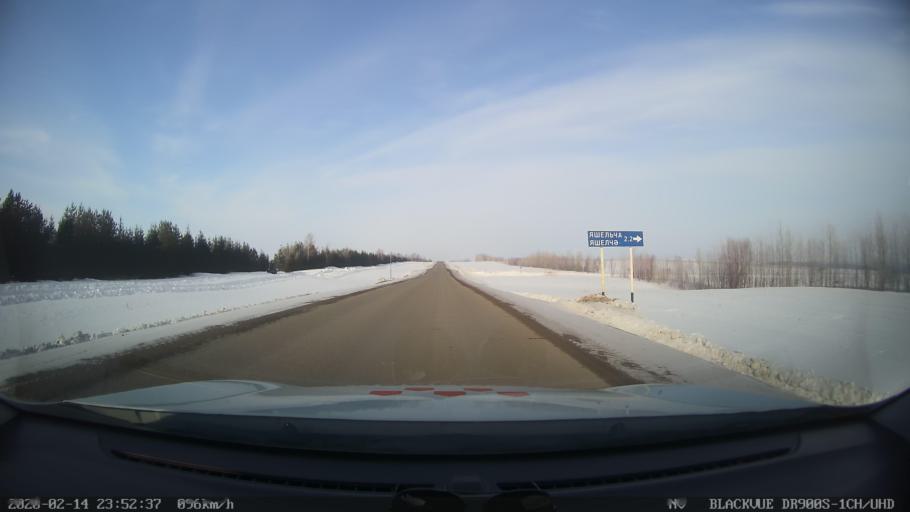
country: RU
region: Tatarstan
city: Kuybyshevskiy Zaton
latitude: 55.2812
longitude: 49.1439
